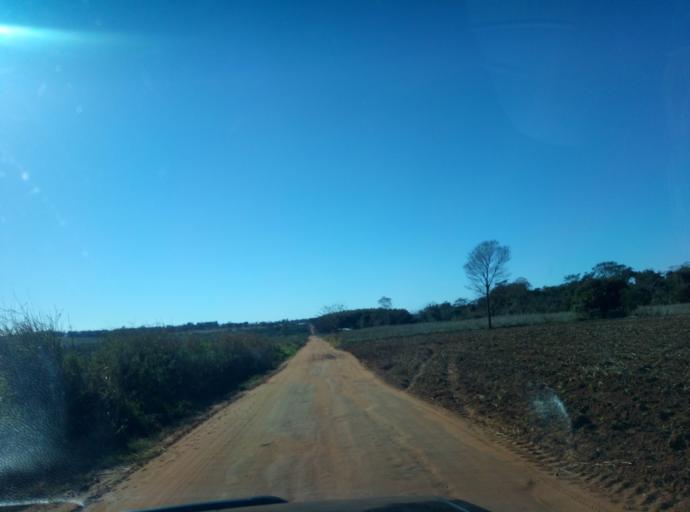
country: PY
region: Caaguazu
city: Doctor Cecilio Baez
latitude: -25.1624
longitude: -56.2668
